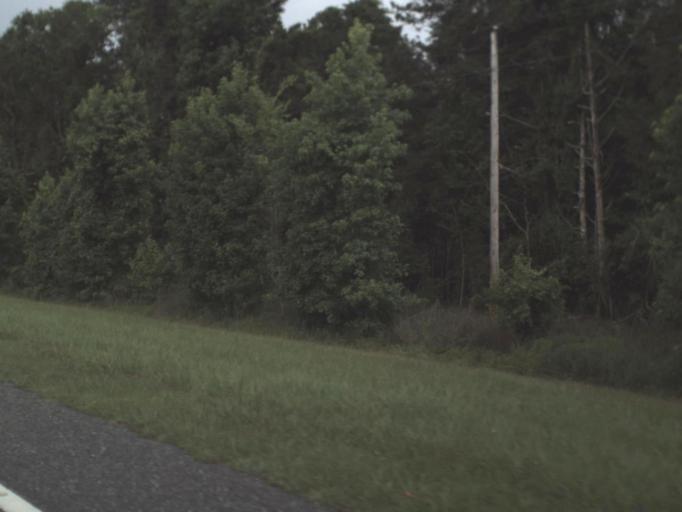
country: US
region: Florida
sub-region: Levy County
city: Inglis
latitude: 29.1908
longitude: -82.6853
